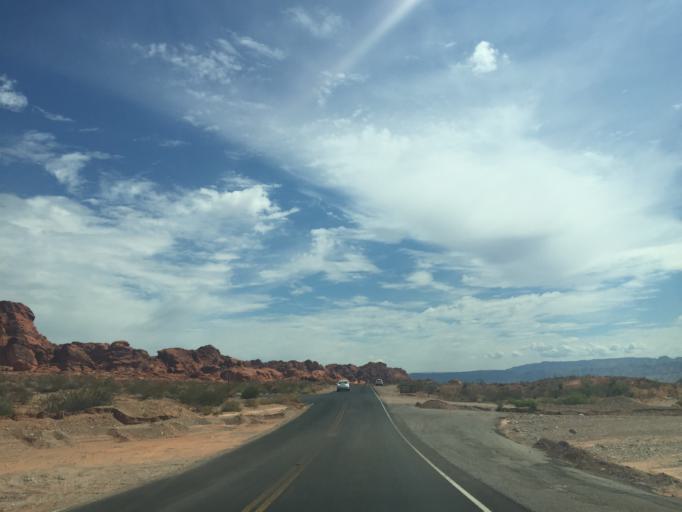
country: US
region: Nevada
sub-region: Clark County
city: Moapa Valley
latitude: 36.4264
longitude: -114.5145
